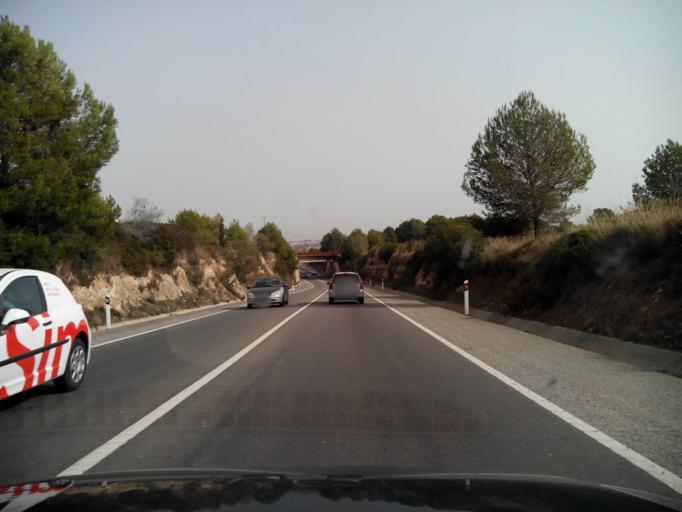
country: ES
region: Catalonia
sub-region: Provincia de Tarragona
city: El Vendrell
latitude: 41.1830
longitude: 1.5088
